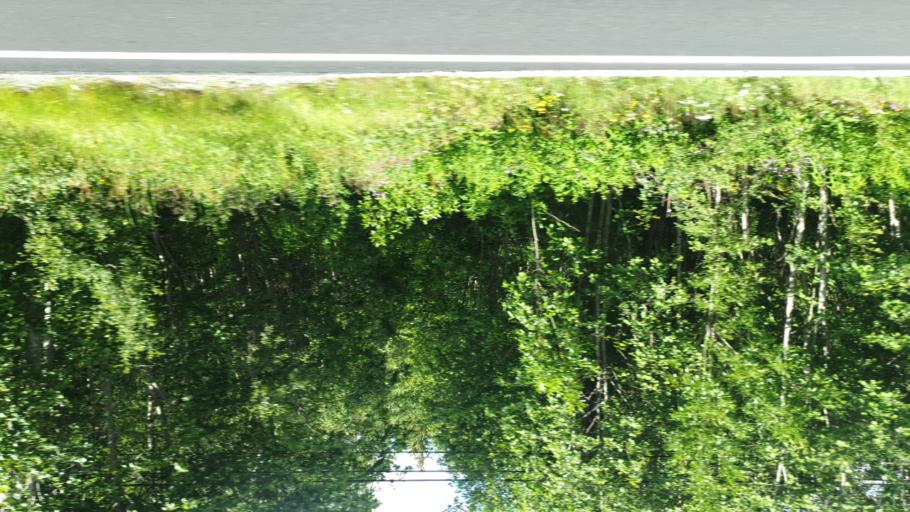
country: NO
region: Oppland
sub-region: Oystre Slidre
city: Heggenes
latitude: 61.1795
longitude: 8.9985
